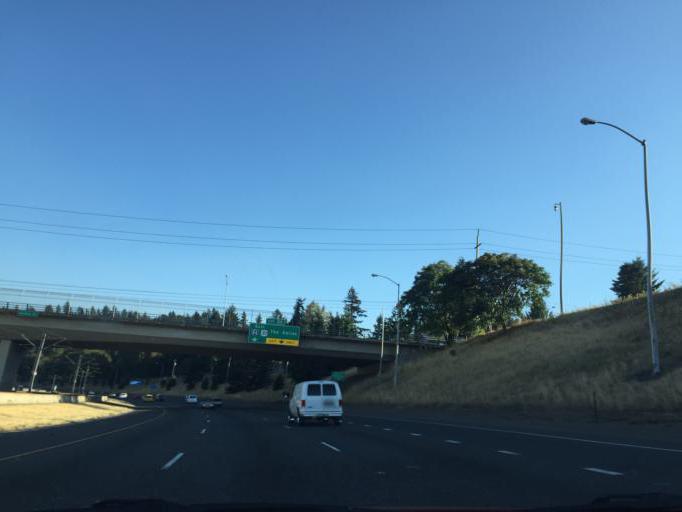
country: US
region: Oregon
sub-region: Multnomah County
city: Lents
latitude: 45.5564
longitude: -122.5673
